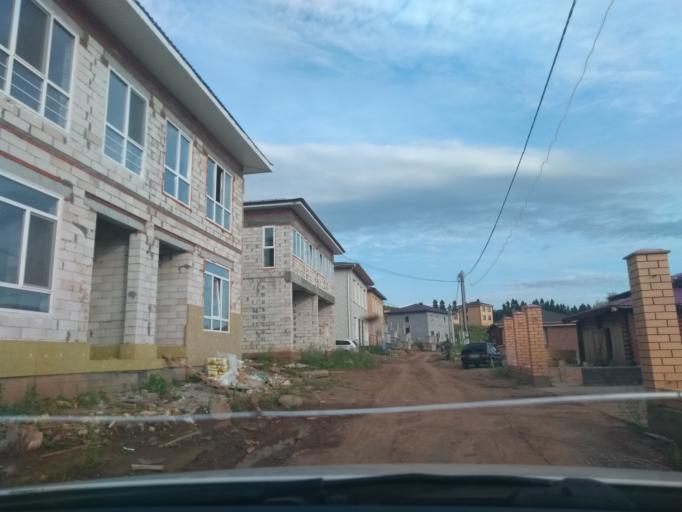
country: RU
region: Perm
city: Perm
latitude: 58.0008
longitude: 56.3200
